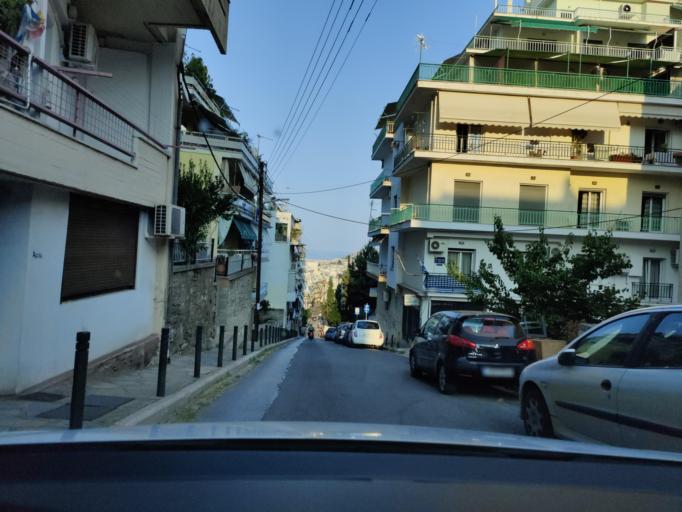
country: GR
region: East Macedonia and Thrace
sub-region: Nomos Kavalas
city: Kavala
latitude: 40.9392
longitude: 24.3989
